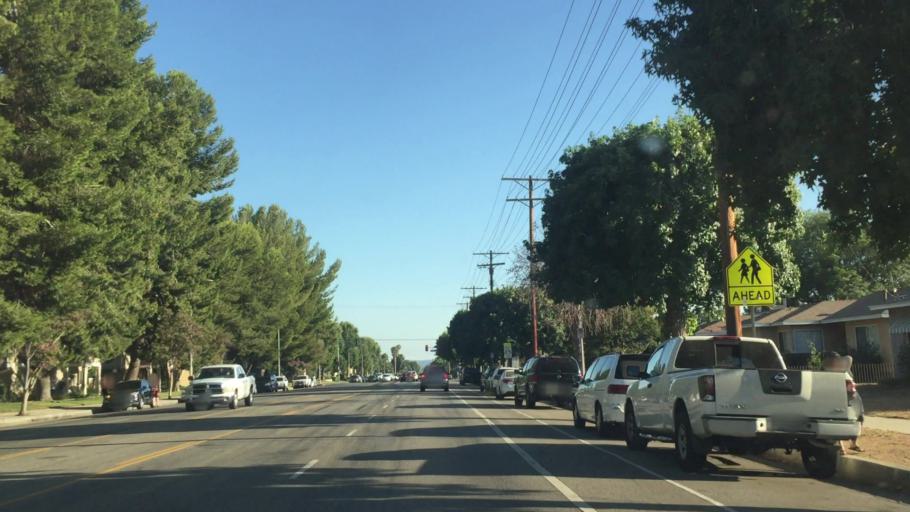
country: US
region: California
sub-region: Los Angeles County
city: San Fernando
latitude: 34.2662
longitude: -118.4849
